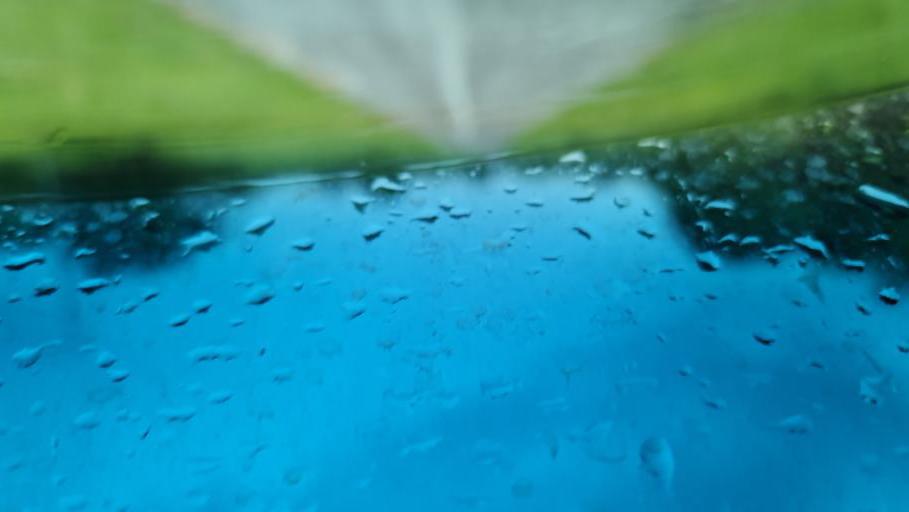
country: MZ
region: Nampula
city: Antonio Enes
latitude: -15.9284
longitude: 39.4802
